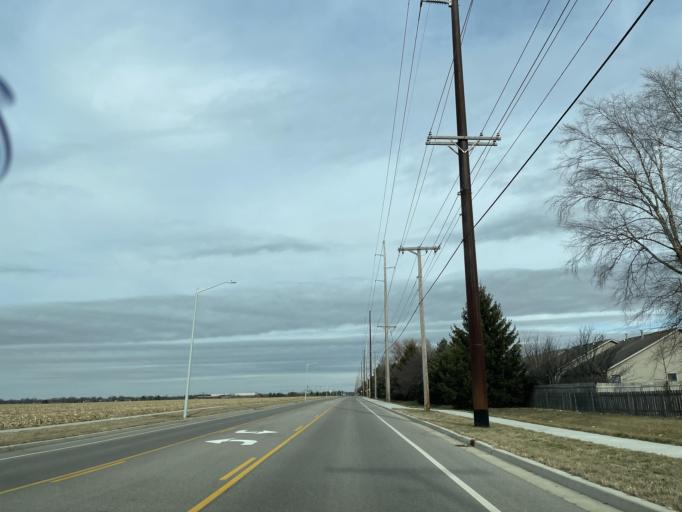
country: US
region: Illinois
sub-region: Sangamon County
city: Jerome
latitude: 39.7617
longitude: -89.7345
